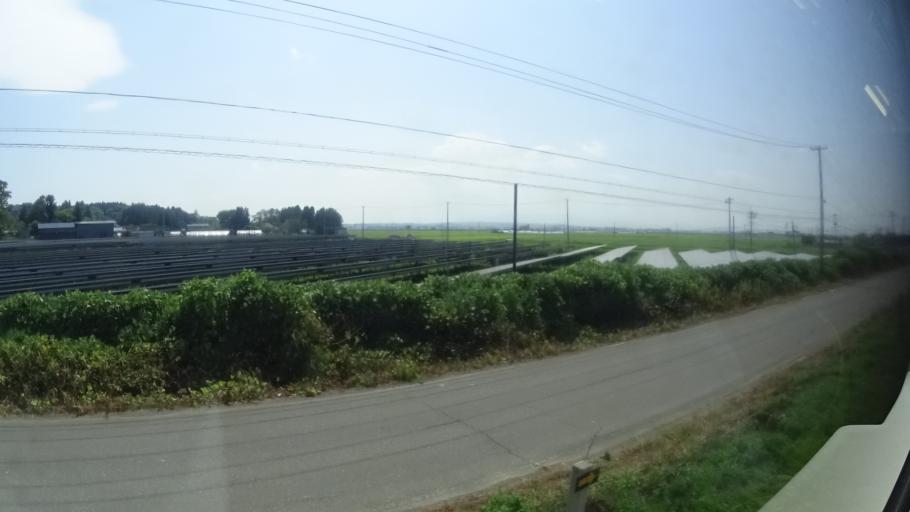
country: JP
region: Miyagi
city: Wakuya
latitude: 38.5273
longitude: 141.1488
